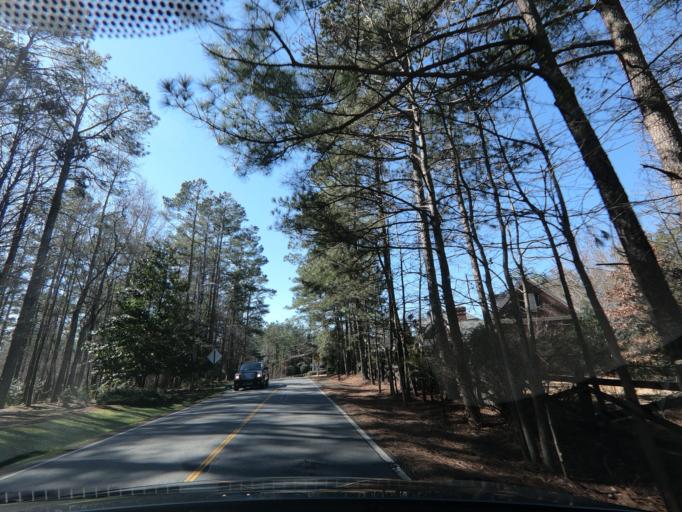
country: US
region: Georgia
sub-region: Cobb County
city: Marietta
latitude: 33.9775
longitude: -84.5900
